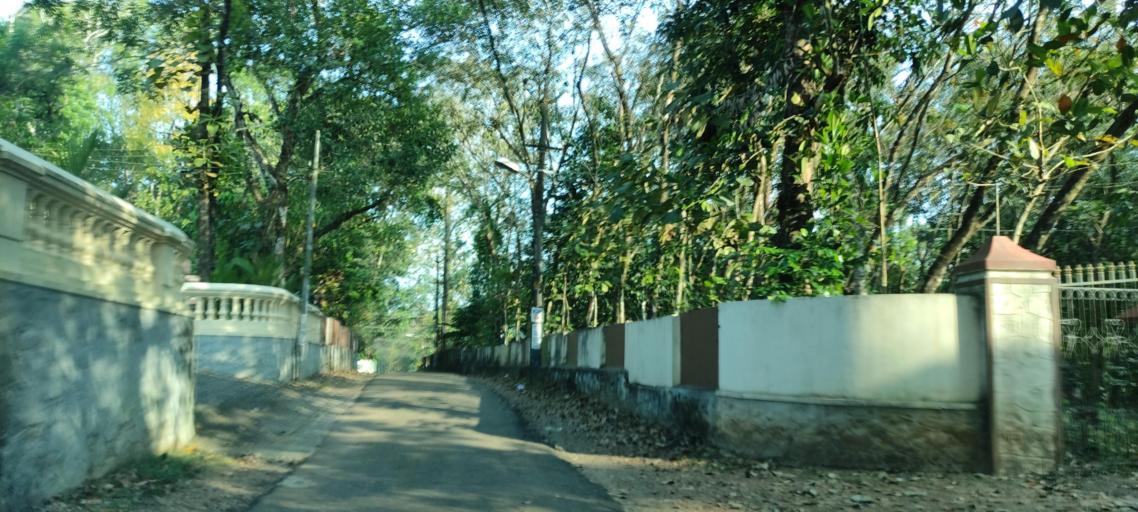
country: IN
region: Kerala
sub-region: Pattanamtitta
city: Adur
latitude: 9.1560
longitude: 76.7441
